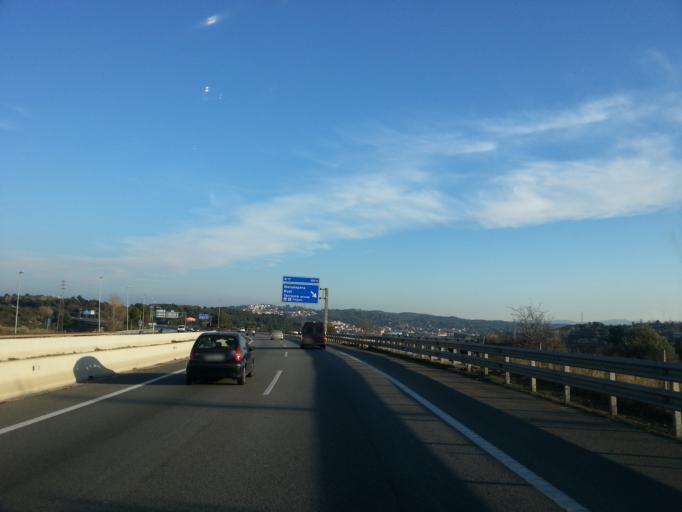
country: ES
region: Catalonia
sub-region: Provincia de Barcelona
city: Terrassa
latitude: 41.5431
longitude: 2.0156
